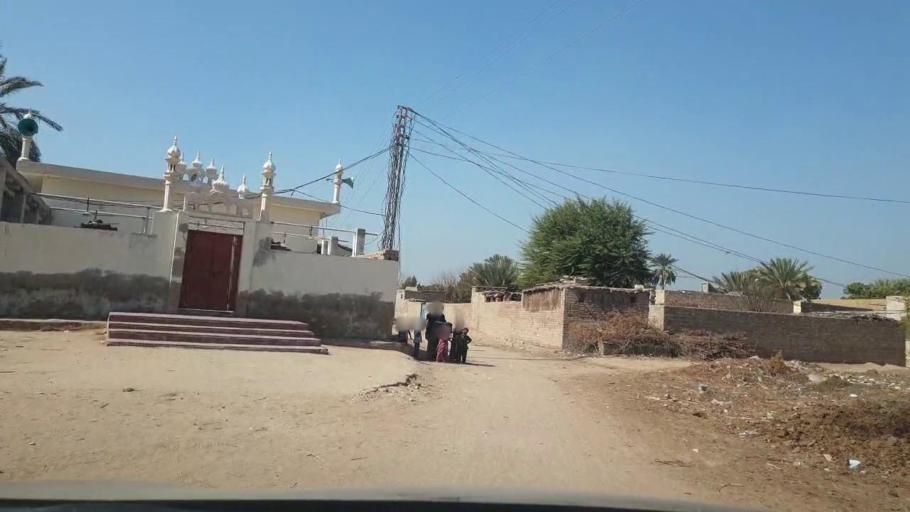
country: PK
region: Sindh
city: Tando Adam
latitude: 25.6372
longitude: 68.6745
